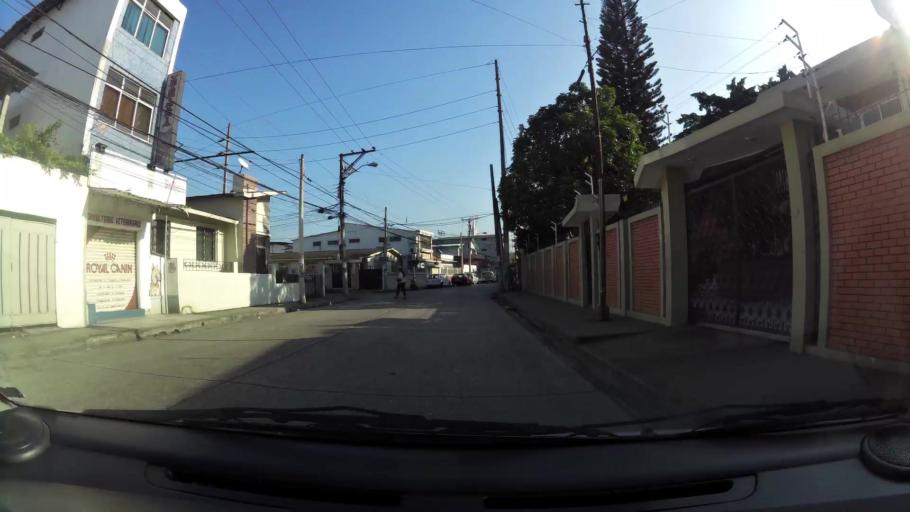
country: EC
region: Guayas
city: Guayaquil
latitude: -2.1606
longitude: -79.9037
